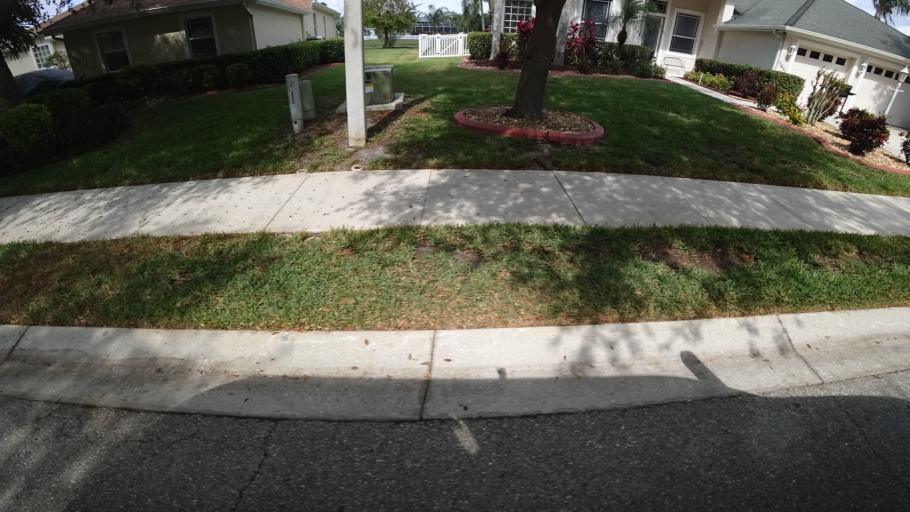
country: US
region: Florida
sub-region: Manatee County
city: Ellenton
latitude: 27.5363
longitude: -82.4454
